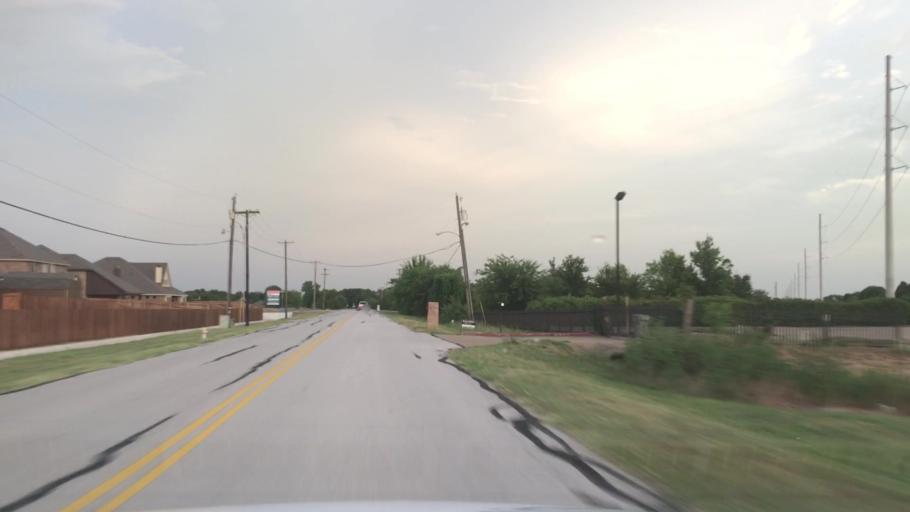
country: US
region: Texas
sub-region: Dallas County
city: Seagoville
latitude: 32.6968
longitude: -96.5581
